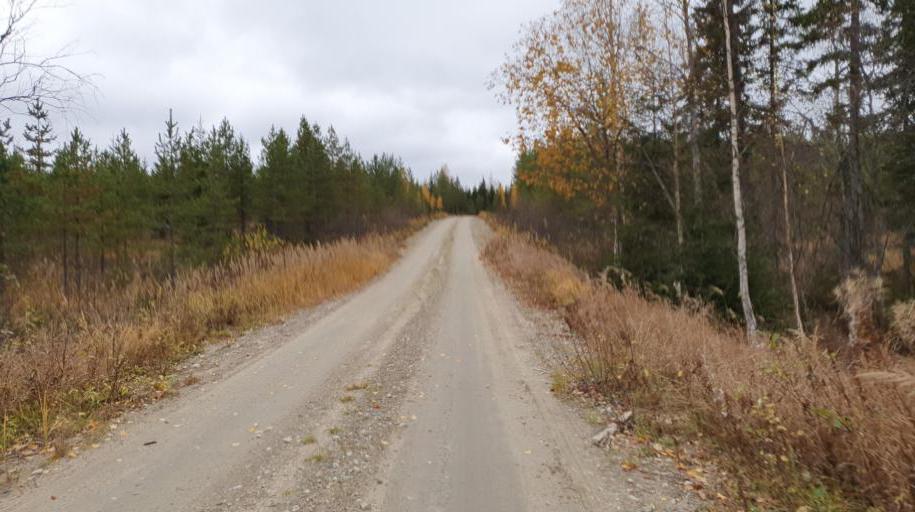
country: FI
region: Kainuu
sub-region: Kehys-Kainuu
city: Kuhmo
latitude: 64.4579
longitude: 29.6057
